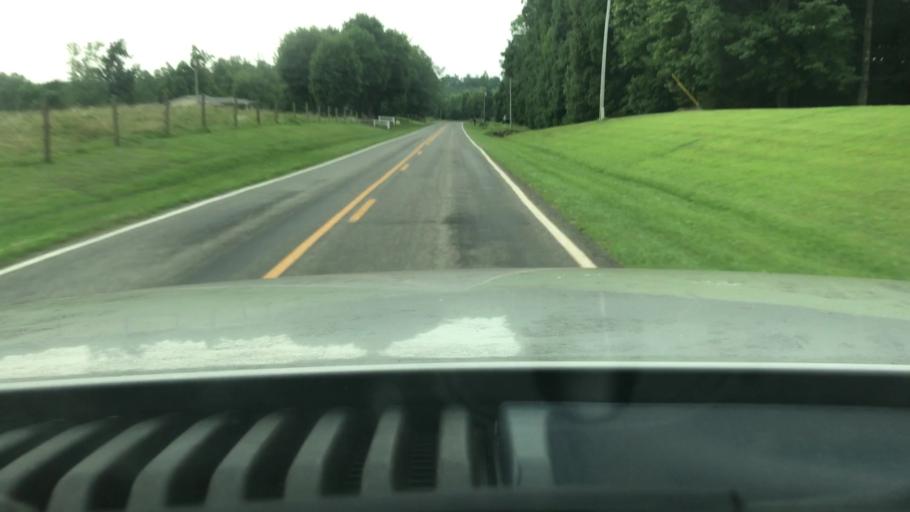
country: US
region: North Carolina
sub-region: Surry County
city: Dobson
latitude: 36.4161
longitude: -80.8208
